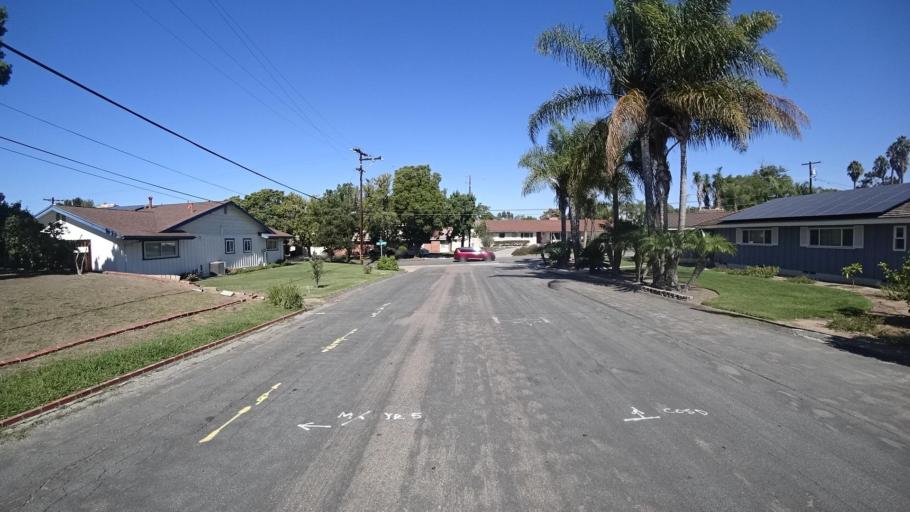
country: US
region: California
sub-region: San Diego County
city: Chula Vista
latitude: 32.6394
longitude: -117.0629
